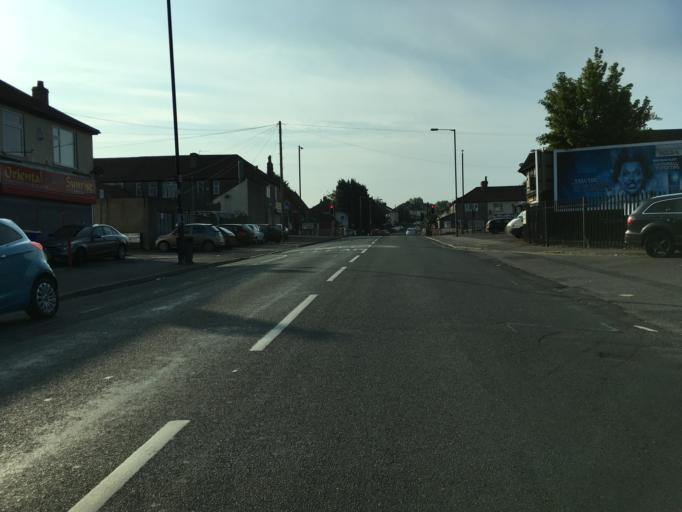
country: GB
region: England
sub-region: Bristol
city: Bristol
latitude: 51.4977
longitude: -2.5982
